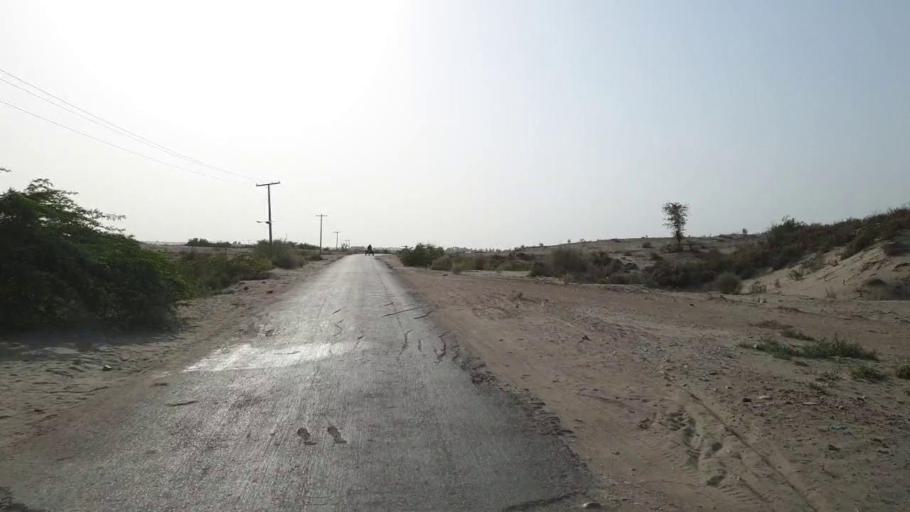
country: PK
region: Sindh
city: Jam Sahib
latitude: 26.4369
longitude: 68.8702
